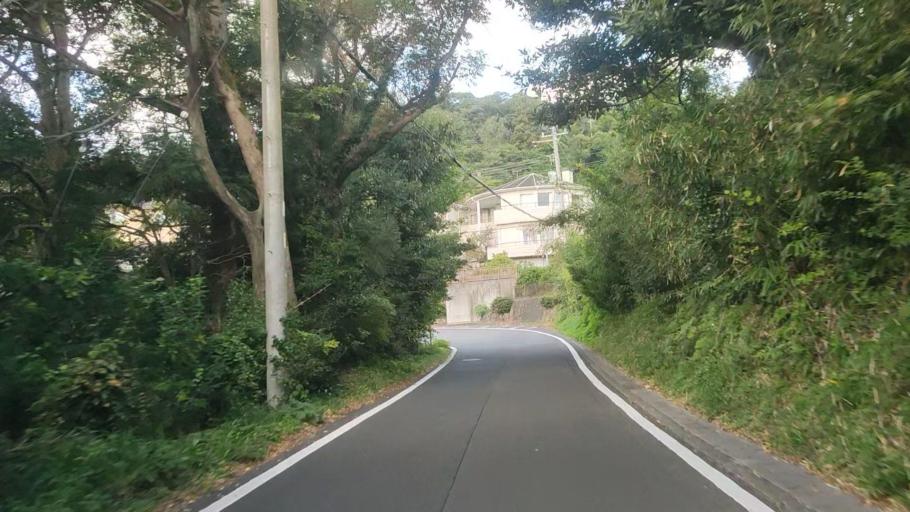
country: JP
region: Shizuoka
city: Ito
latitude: 34.9592
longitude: 139.0806
